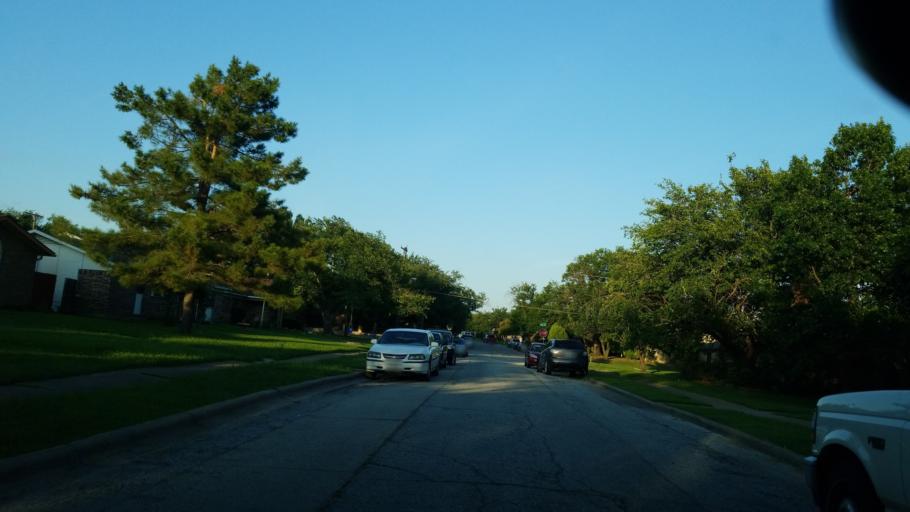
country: US
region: Texas
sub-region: Dallas County
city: Carrollton
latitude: 32.9497
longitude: -96.8826
